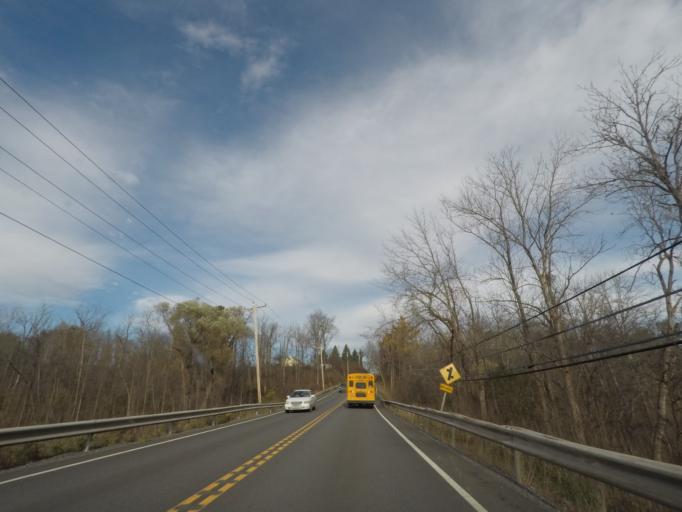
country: US
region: New York
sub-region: Albany County
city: Delmar
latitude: 42.6027
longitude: -73.8823
